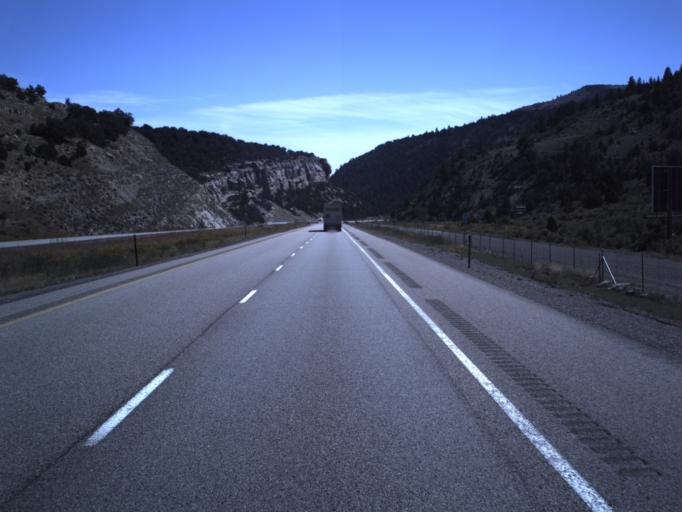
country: US
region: Utah
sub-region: Wayne County
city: Loa
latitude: 38.7611
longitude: -111.4574
